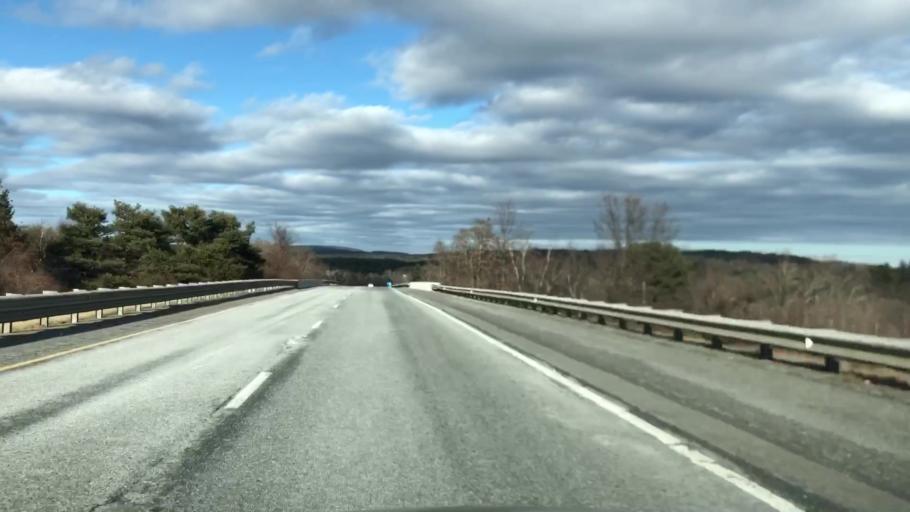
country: US
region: Massachusetts
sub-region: Worcester County
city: West Boylston
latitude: 42.4084
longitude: -71.7947
